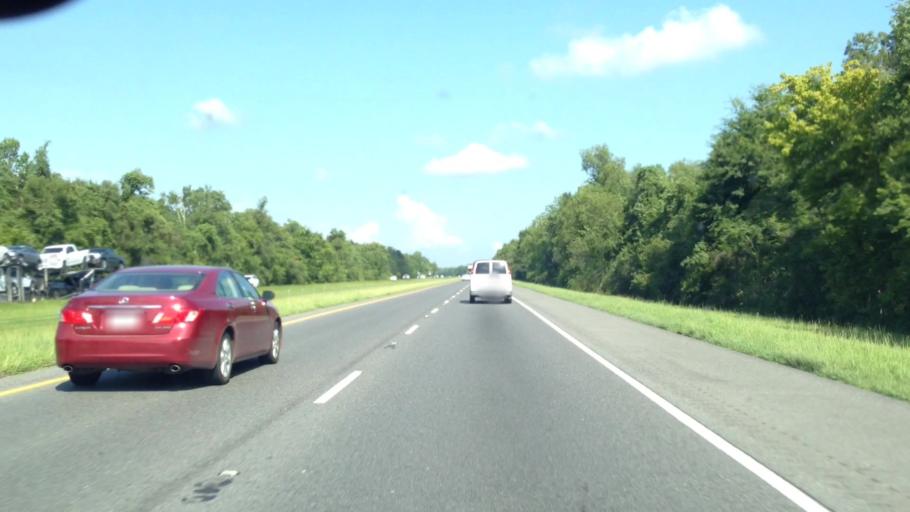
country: US
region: Louisiana
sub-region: Saint James Parish
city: Grand Point
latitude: 30.1451
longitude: -90.7636
